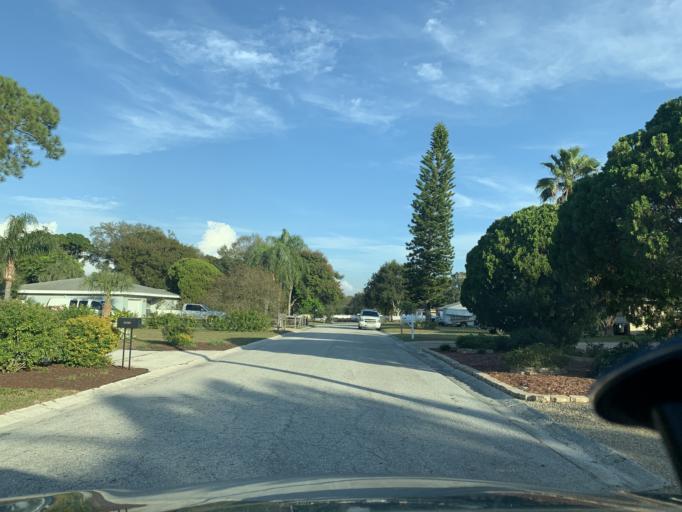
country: US
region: Florida
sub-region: Pinellas County
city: Ridgecrest
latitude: 27.8771
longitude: -82.7973
